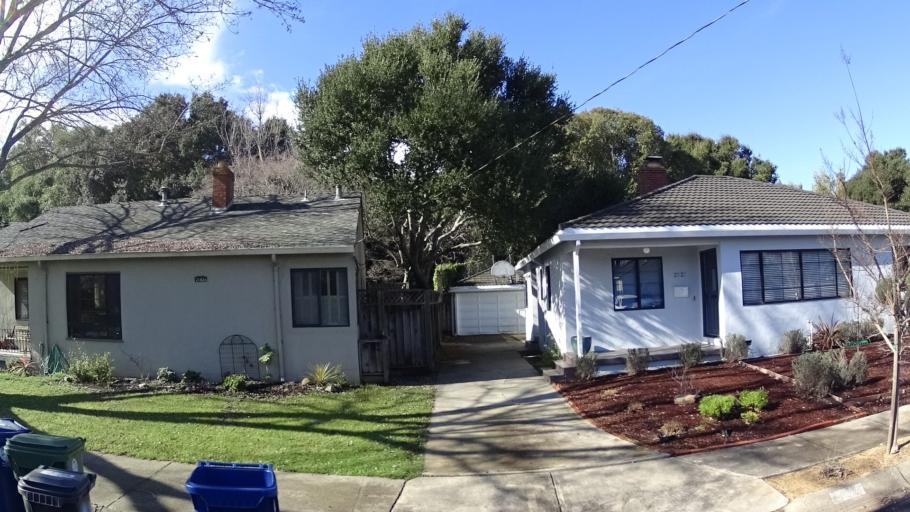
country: US
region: California
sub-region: Alameda County
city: Castro Valley
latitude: 37.6838
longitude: -122.0812
